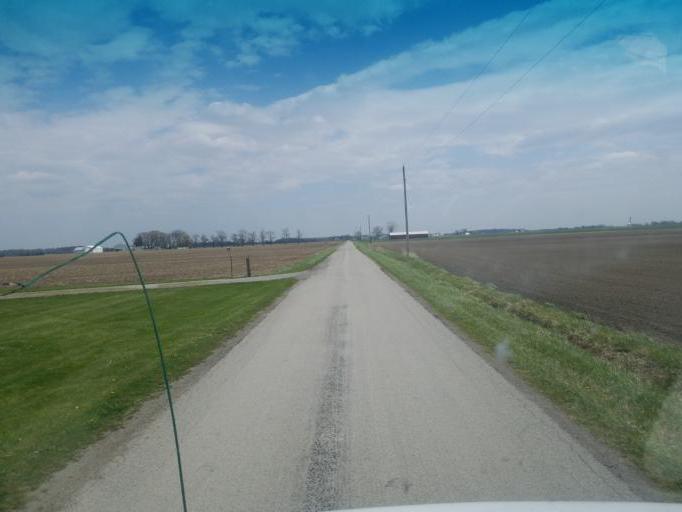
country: US
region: Ohio
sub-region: Wyandot County
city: Upper Sandusky
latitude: 40.7739
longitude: -83.3458
